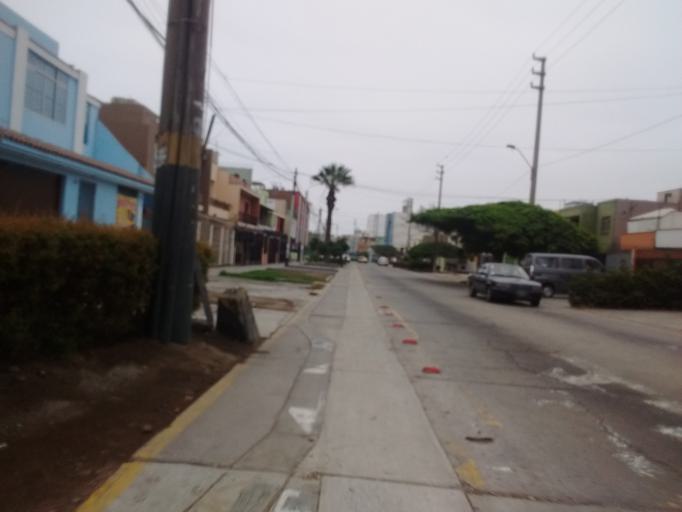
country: PE
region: Lima
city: Lima
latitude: -12.0684
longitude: -77.0549
